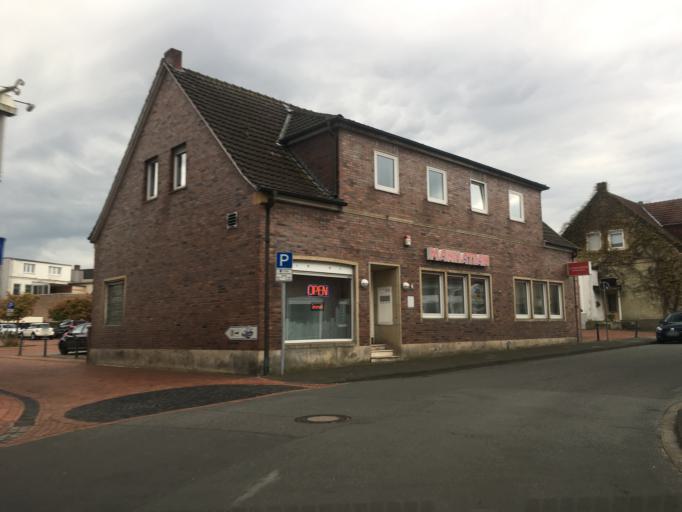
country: DE
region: North Rhine-Westphalia
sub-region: Regierungsbezirk Munster
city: Steinfurt
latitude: 52.1255
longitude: 7.3938
